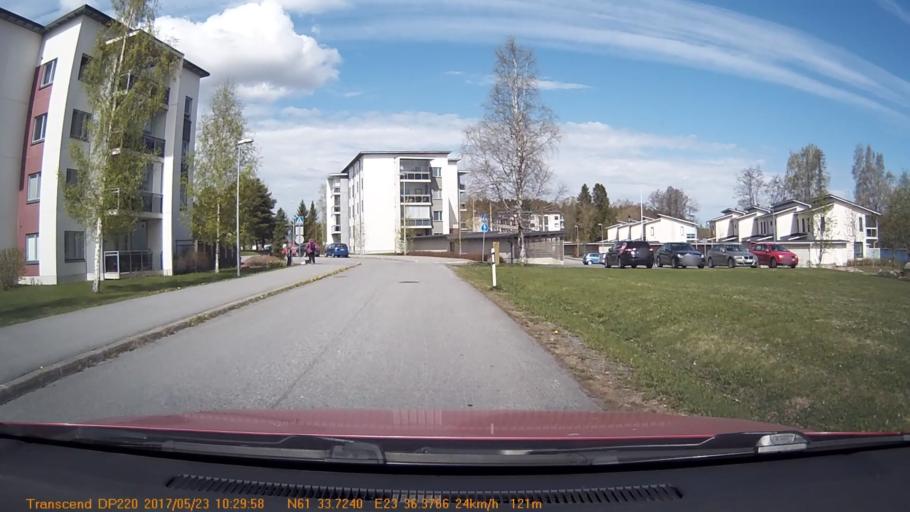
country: FI
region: Pirkanmaa
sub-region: Tampere
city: Yloejaervi
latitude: 61.5620
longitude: 23.6060
